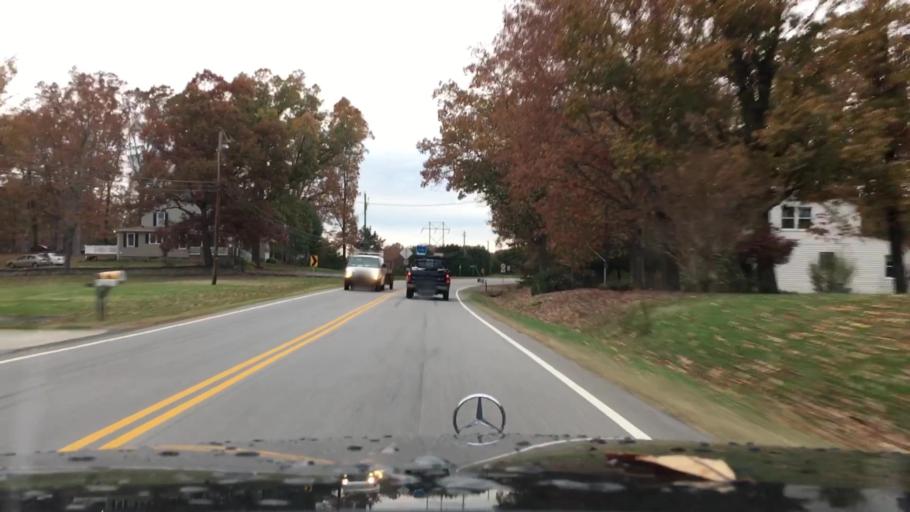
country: US
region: Virginia
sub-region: Campbell County
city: Altavista
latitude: 37.1402
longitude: -79.3067
